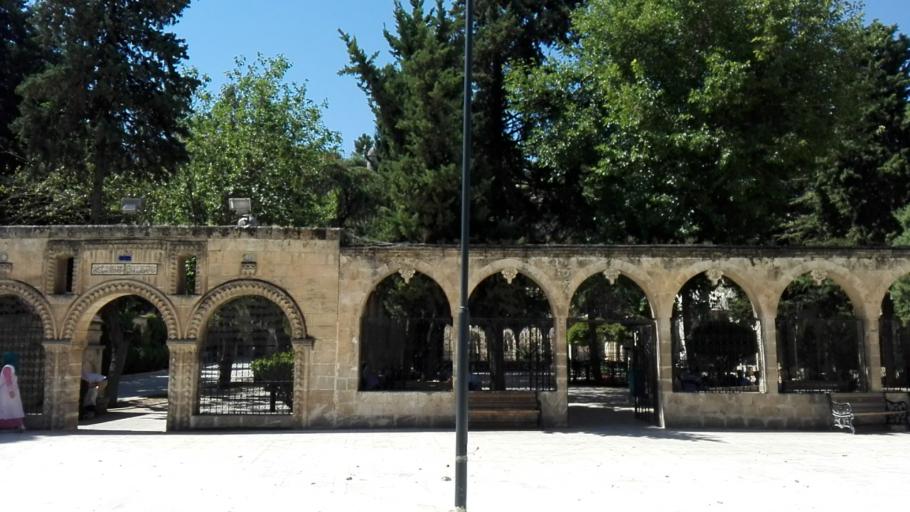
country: TR
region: Sanliurfa
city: Sanliurfa
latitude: 37.1473
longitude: 38.7868
